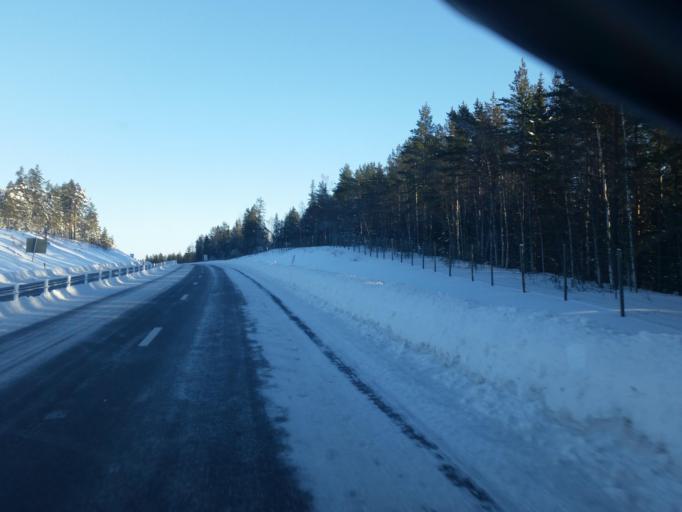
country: SE
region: Norrbotten
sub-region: Pitea Kommun
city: Pitea
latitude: 65.1032
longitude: 21.5131
